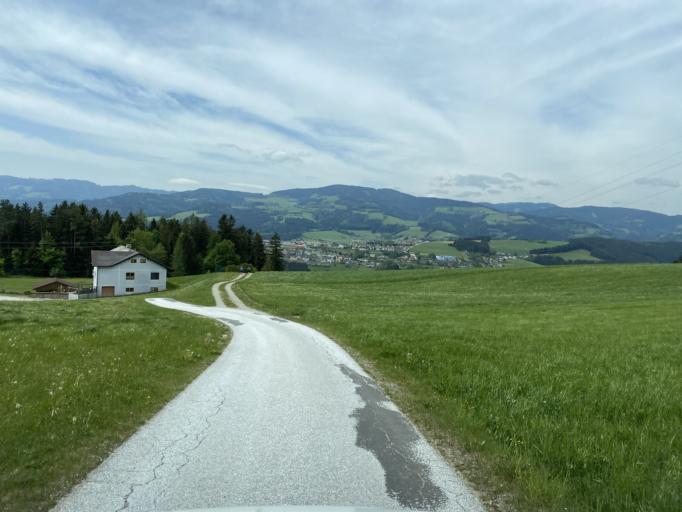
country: AT
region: Styria
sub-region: Politischer Bezirk Weiz
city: Gschaid bei Birkfeld
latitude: 47.3552
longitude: 15.7165
